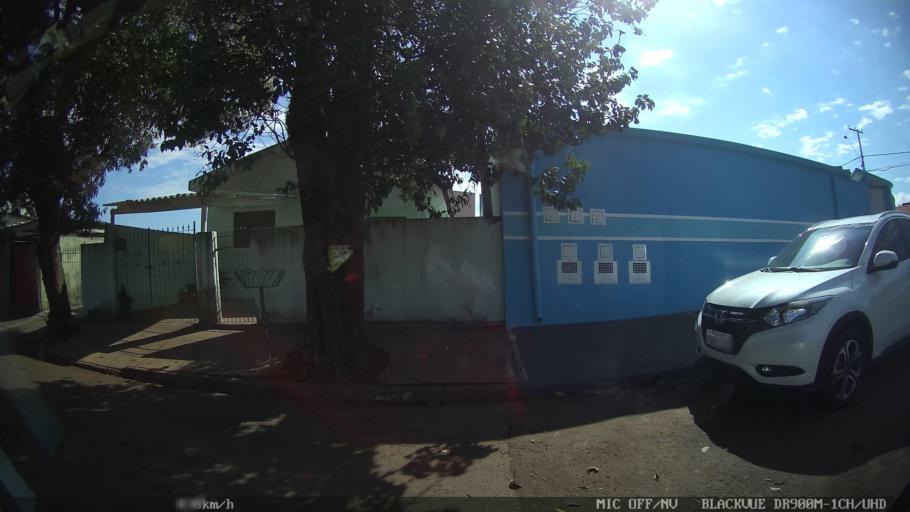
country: BR
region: Sao Paulo
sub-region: Americana
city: Americana
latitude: -22.7386
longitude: -47.3003
